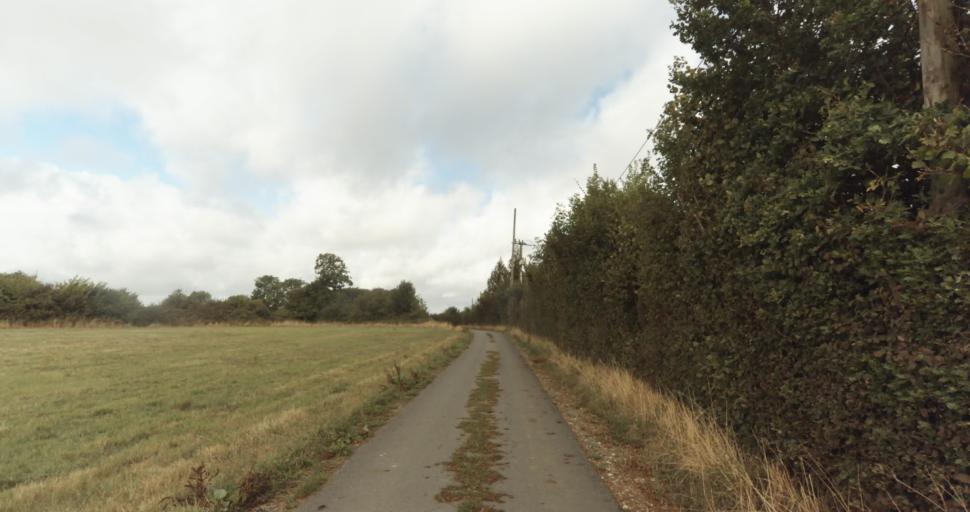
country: FR
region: Lower Normandy
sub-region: Departement de l'Orne
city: Gace
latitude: 48.8428
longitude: 0.3130
